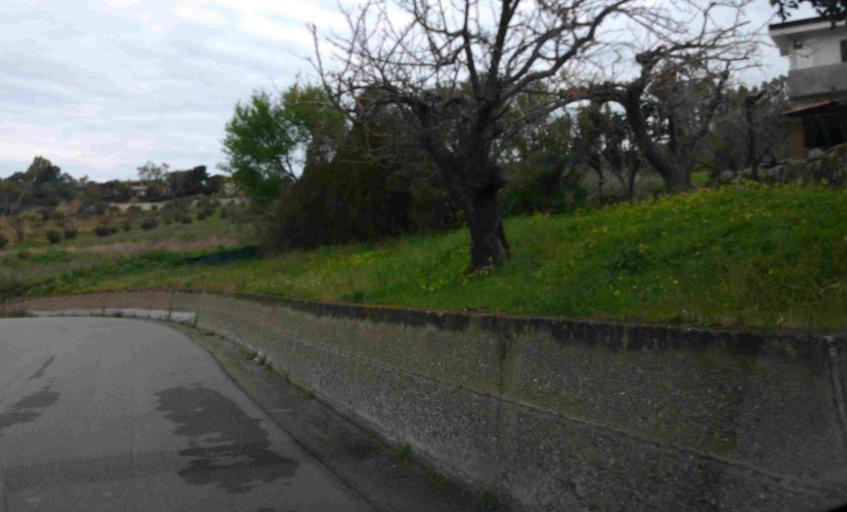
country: IT
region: Calabria
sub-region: Provincia di Catanzaro
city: Sellia Marina
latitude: 38.8874
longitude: 16.7102
